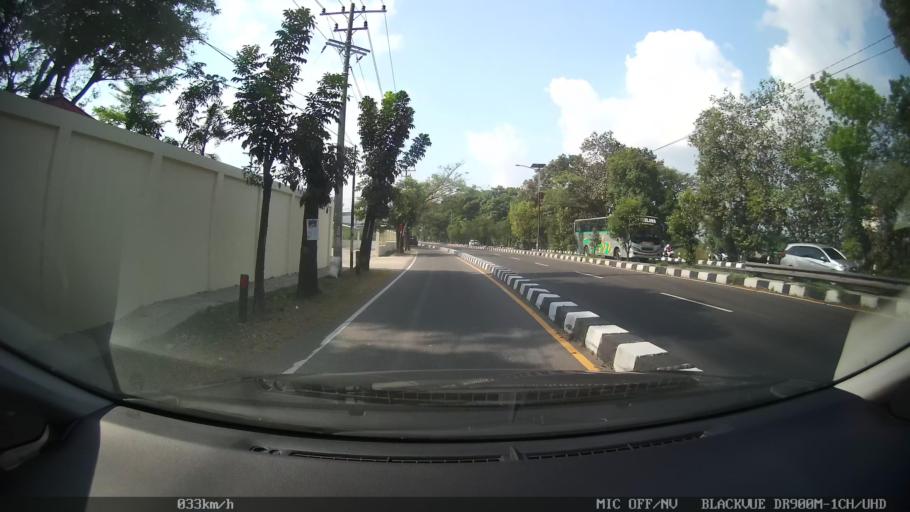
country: ID
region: Daerah Istimewa Yogyakarta
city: Sewon
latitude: -7.8363
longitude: 110.4060
